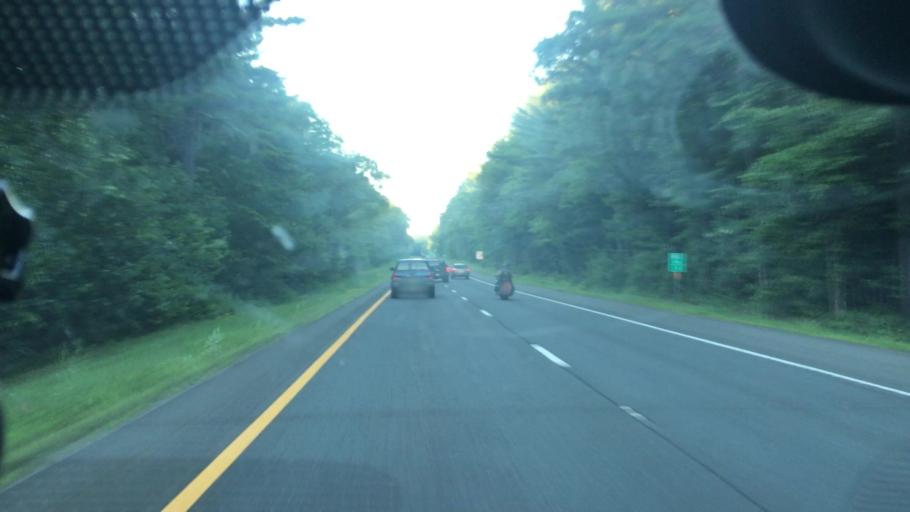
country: US
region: Massachusetts
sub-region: Franklin County
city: Turners Falls
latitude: 42.6239
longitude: -72.5861
